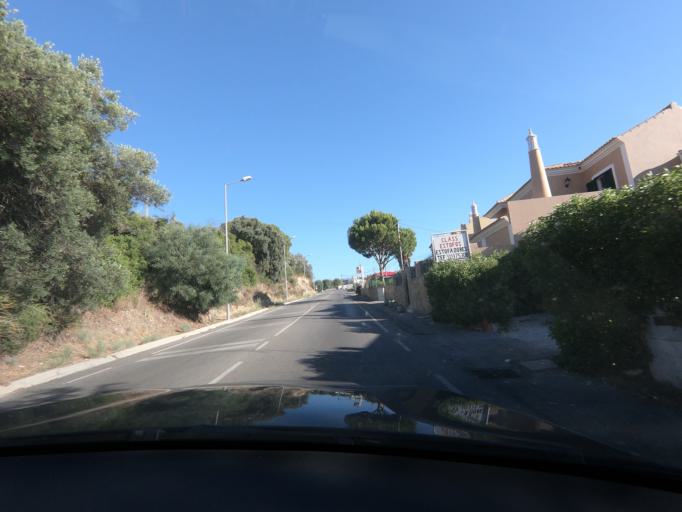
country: PT
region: Faro
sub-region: Loule
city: Loule
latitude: 37.1133
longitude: -8.0080
